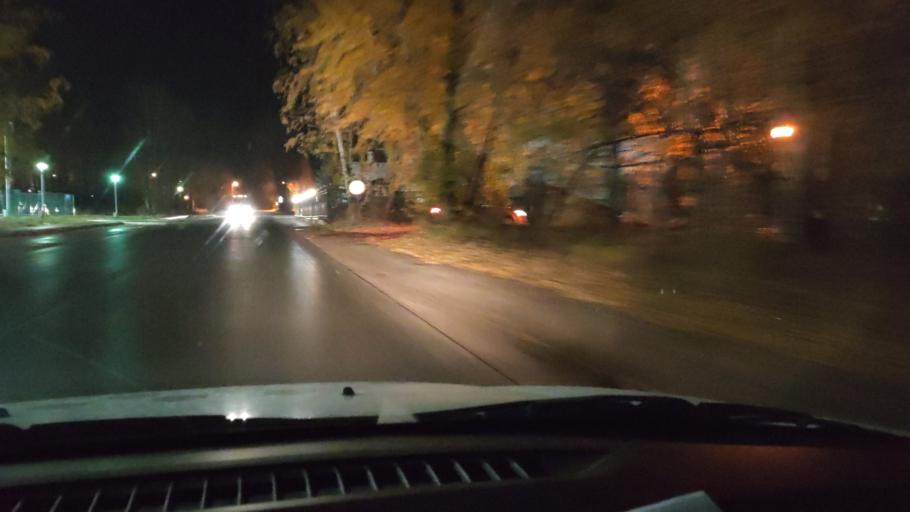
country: RU
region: Perm
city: Overyata
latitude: 58.0181
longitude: 55.9114
